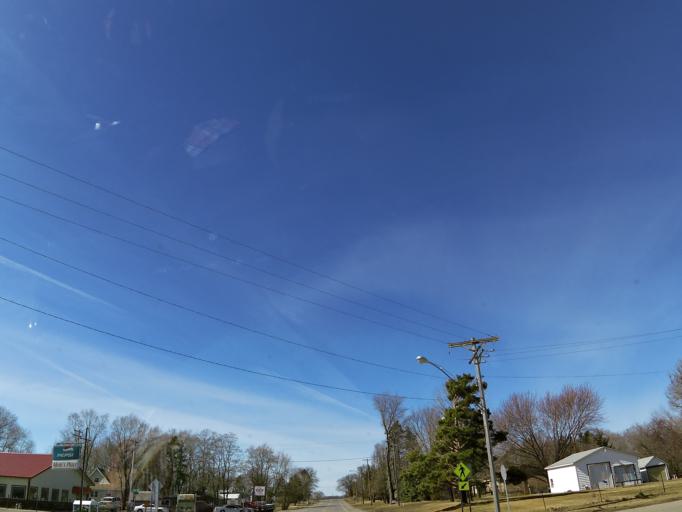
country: US
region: Minnesota
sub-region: Wright County
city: Annandale
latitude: 45.2928
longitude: -94.2147
